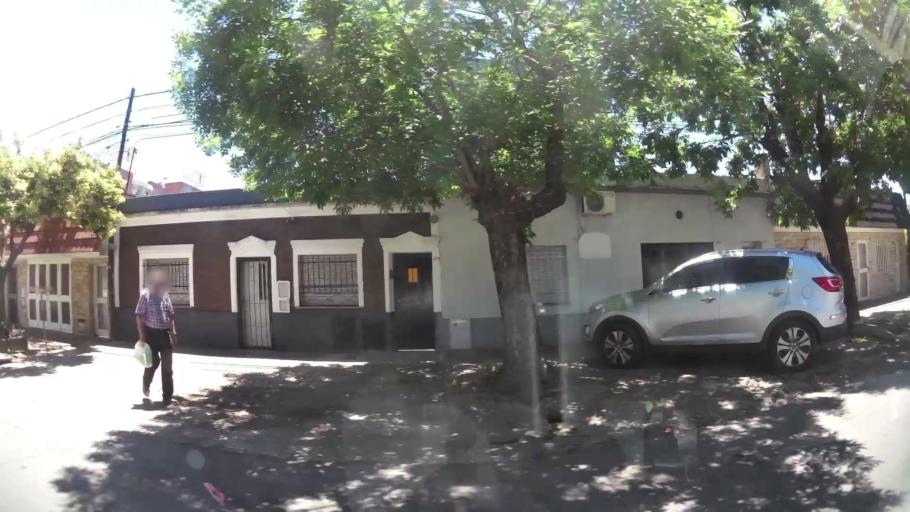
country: AR
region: Santa Fe
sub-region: Departamento de Rosario
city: Rosario
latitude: -32.9507
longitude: -60.6845
